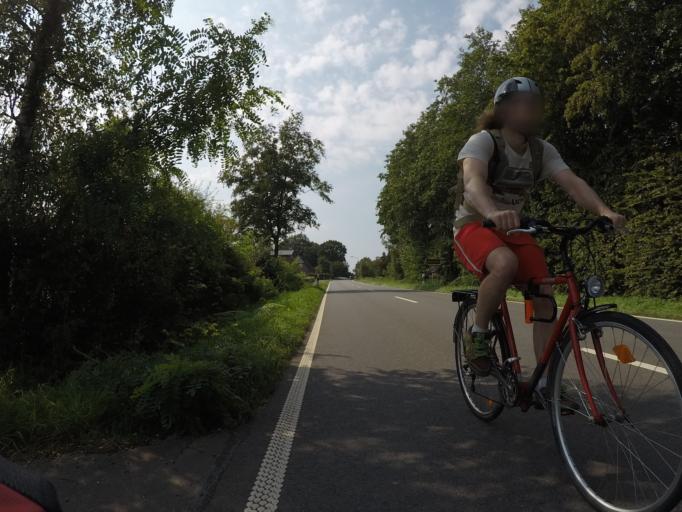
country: DE
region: Schleswig-Holstein
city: Huttblek
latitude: 53.8402
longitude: 10.0481
